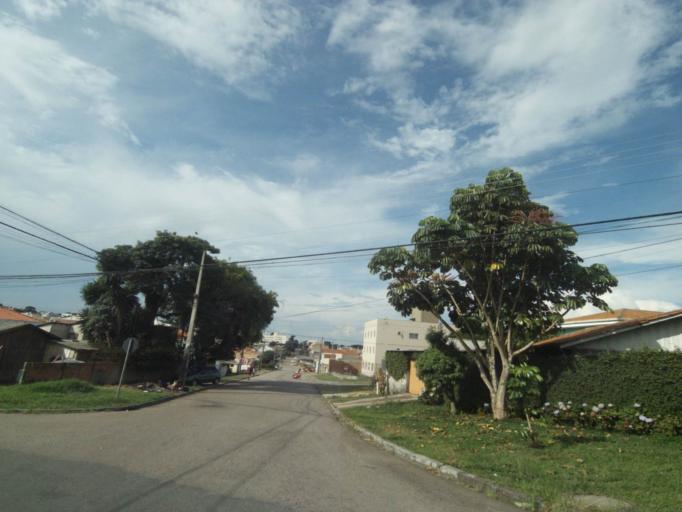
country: BR
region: Parana
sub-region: Pinhais
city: Pinhais
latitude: -25.4509
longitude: -49.2247
